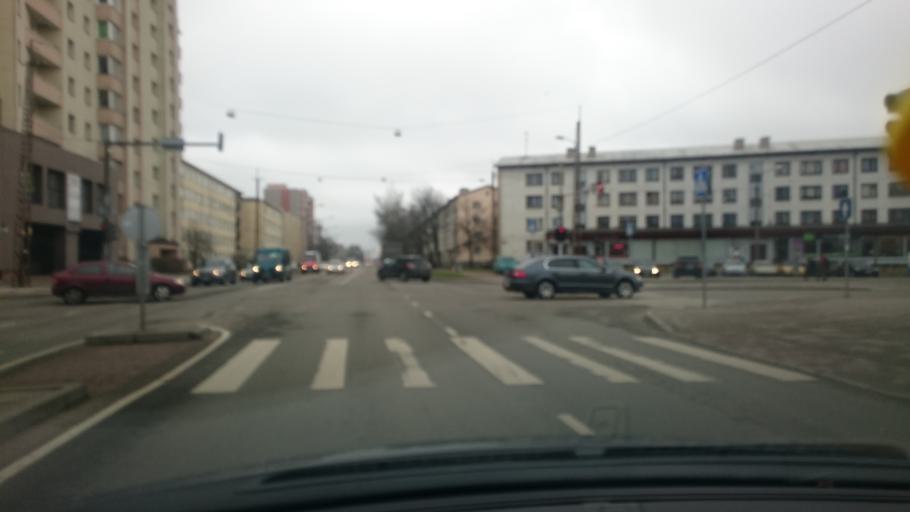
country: EE
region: Harju
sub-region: Tallinna linn
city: Tallinn
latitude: 59.4491
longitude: 24.6980
